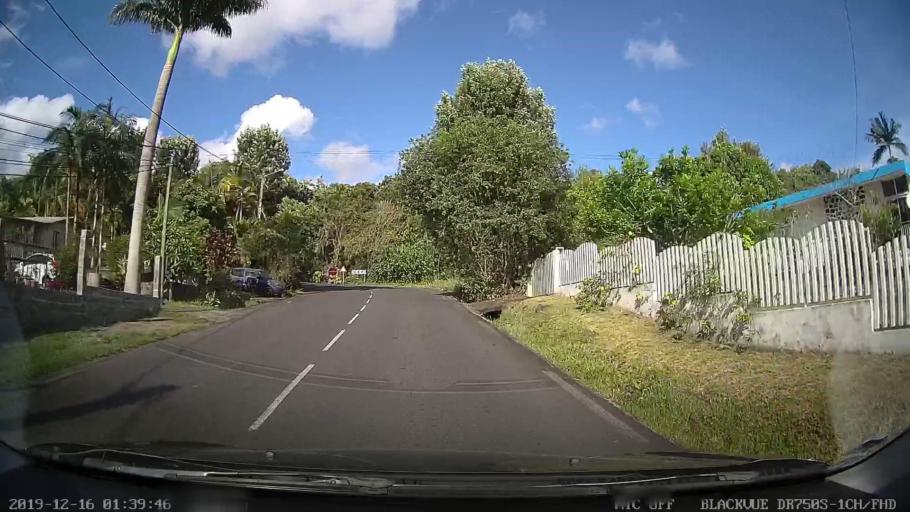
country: RE
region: Reunion
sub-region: Reunion
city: Le Tampon
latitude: -21.2614
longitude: 55.5086
